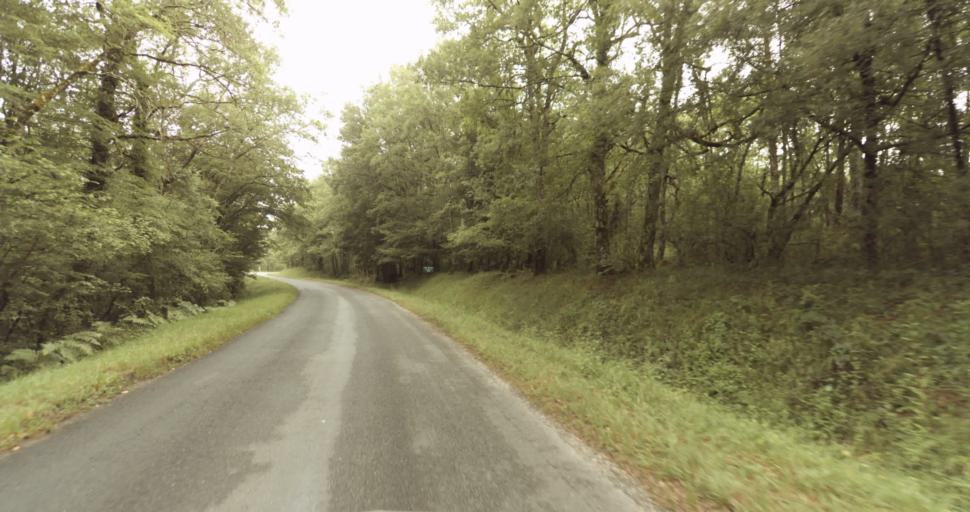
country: FR
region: Aquitaine
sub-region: Departement de la Dordogne
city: Lalinde
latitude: 44.8947
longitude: 0.7703
